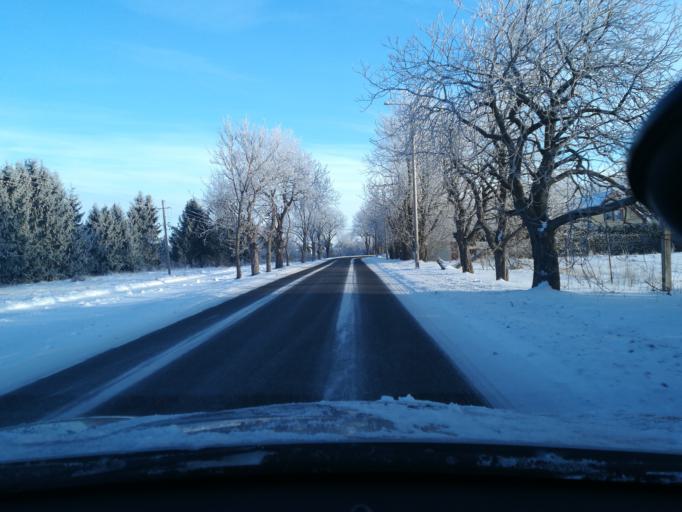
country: EE
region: Harju
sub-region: Keila linn
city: Keila
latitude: 59.3970
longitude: 24.3115
